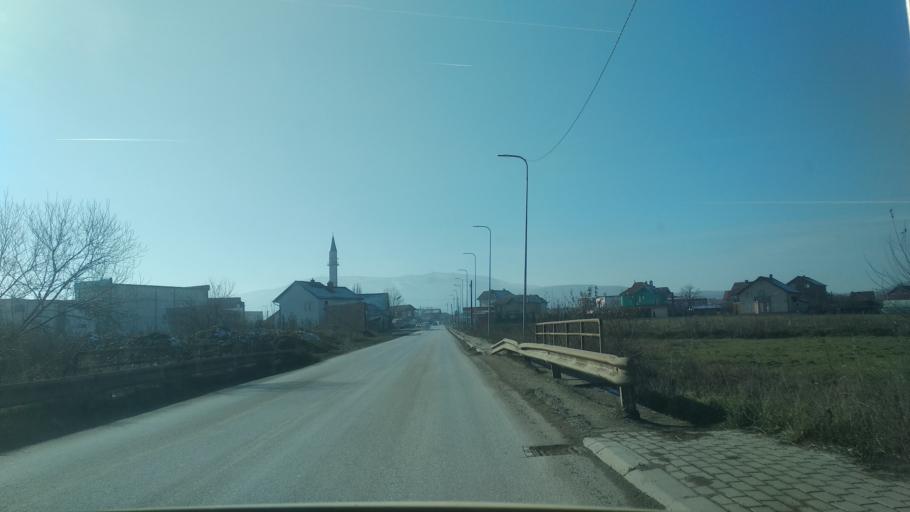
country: XK
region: Pristina
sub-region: Komuna e Gracanices
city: Glanica
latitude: 42.6022
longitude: 21.0258
